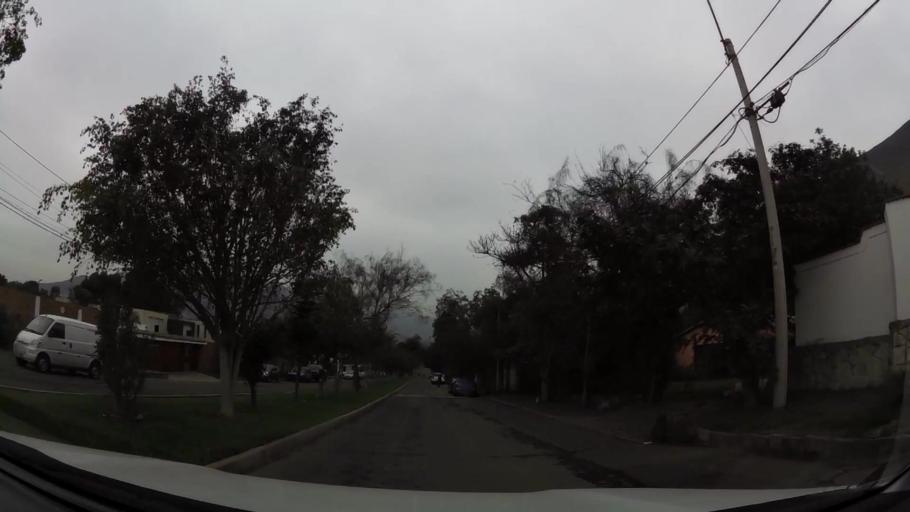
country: PE
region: Lima
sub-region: Lima
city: La Molina
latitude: -12.0905
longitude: -76.9226
